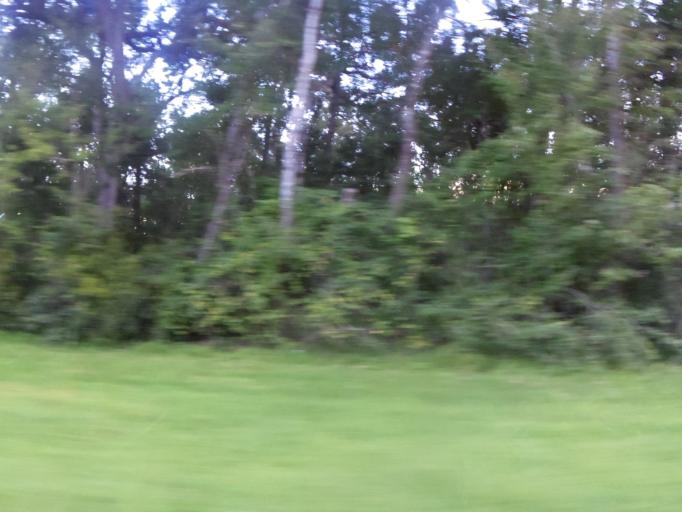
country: US
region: Georgia
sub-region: Camden County
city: St. Marys
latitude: 30.7356
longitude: -81.5508
